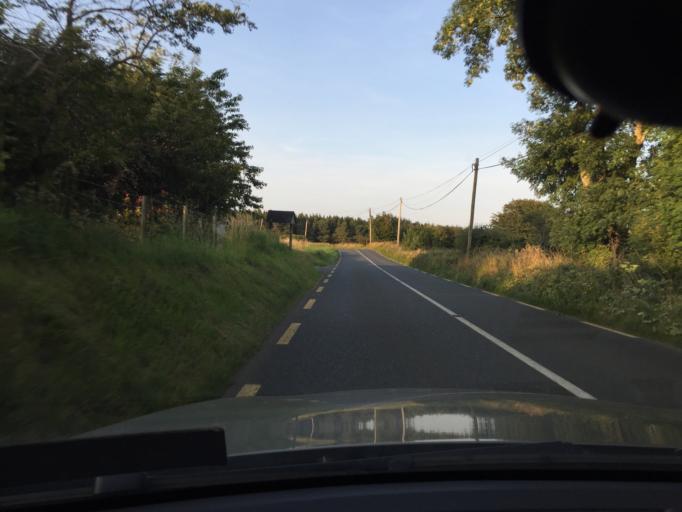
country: IE
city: Newtownmountkennedy
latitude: 53.0911
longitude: -6.2060
